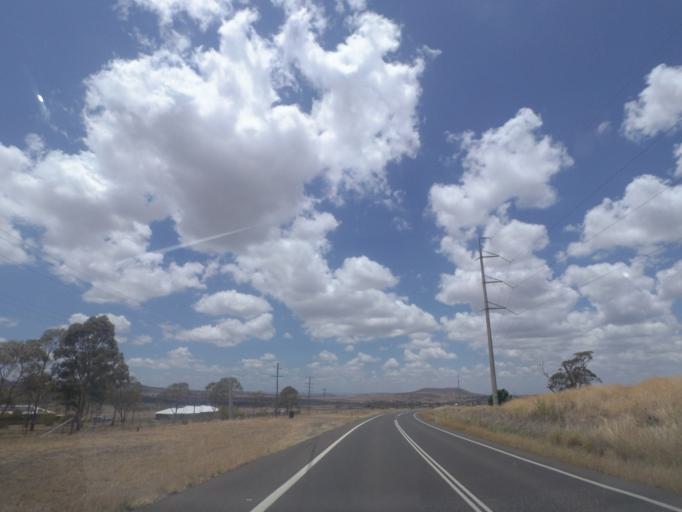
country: AU
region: Queensland
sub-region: Toowoomba
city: Top Camp
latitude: -27.7511
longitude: 151.9335
